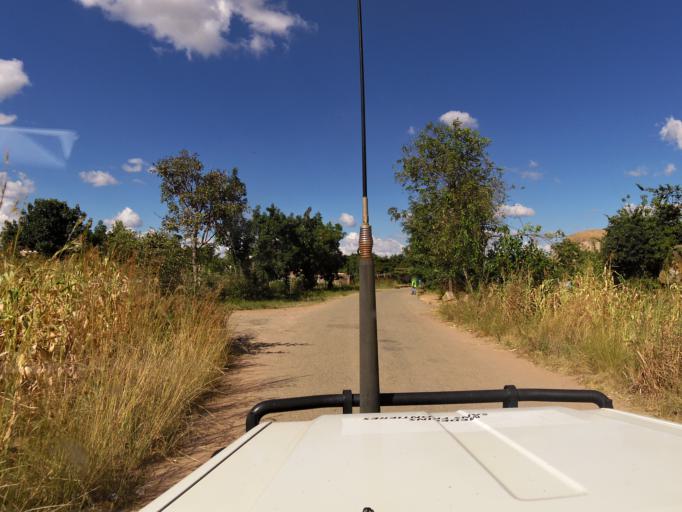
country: ZW
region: Harare
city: Epworth
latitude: -17.8712
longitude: 31.1432
